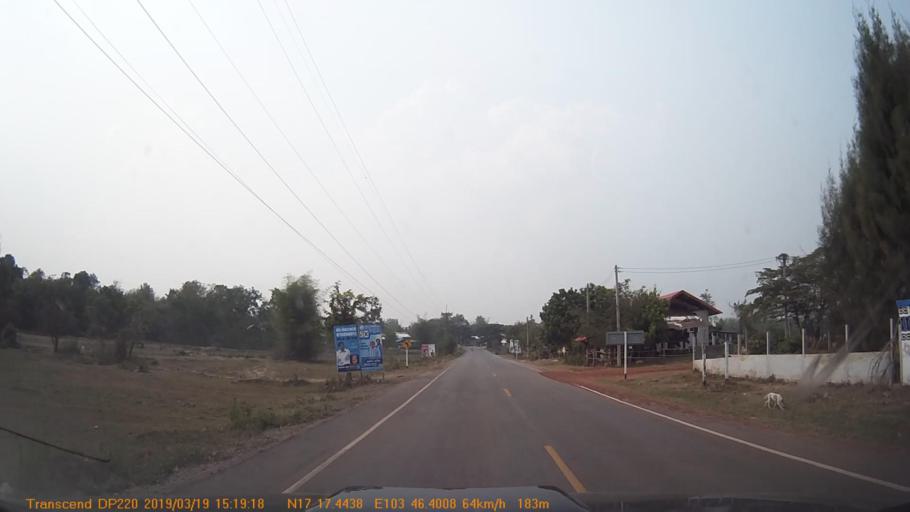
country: TH
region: Sakon Nakhon
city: Phanna Nikhom
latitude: 17.2911
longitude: 103.7732
